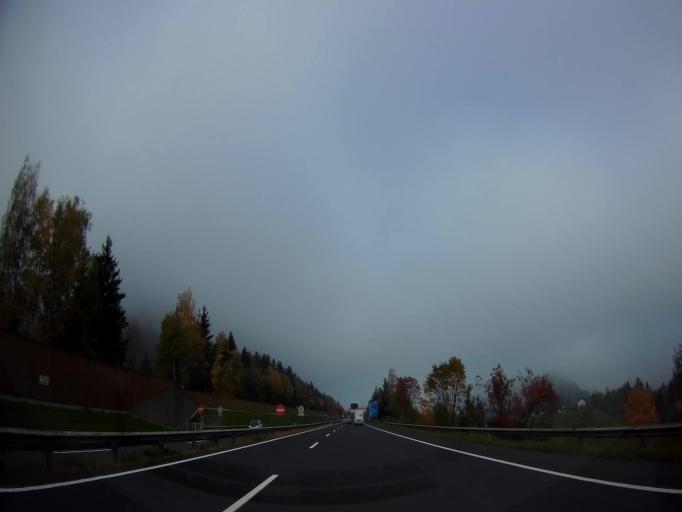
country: AT
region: Styria
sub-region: Politischer Bezirk Leoben
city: Sankt Michael in Obersteiermark
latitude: 47.3265
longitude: 15.0268
